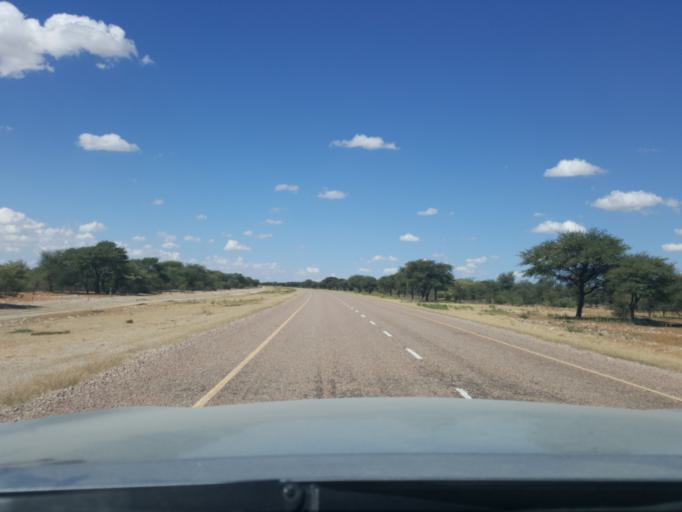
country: BW
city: Lehututu
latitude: -23.9229
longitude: 22.0059
